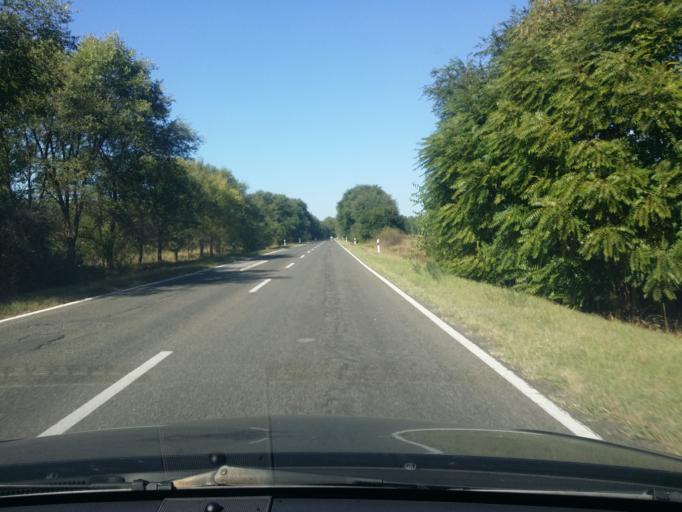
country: HU
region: Bacs-Kiskun
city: Palmonostora
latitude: 46.6172
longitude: 19.9045
